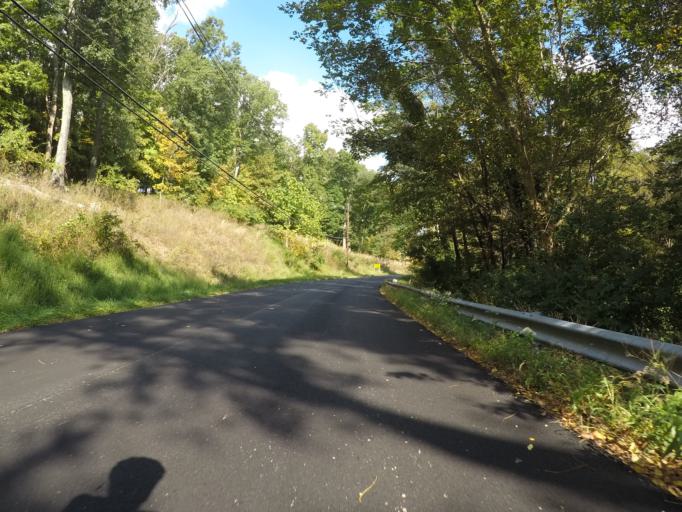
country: US
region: West Virginia
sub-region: Cabell County
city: Huntington
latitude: 38.3882
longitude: -82.4271
